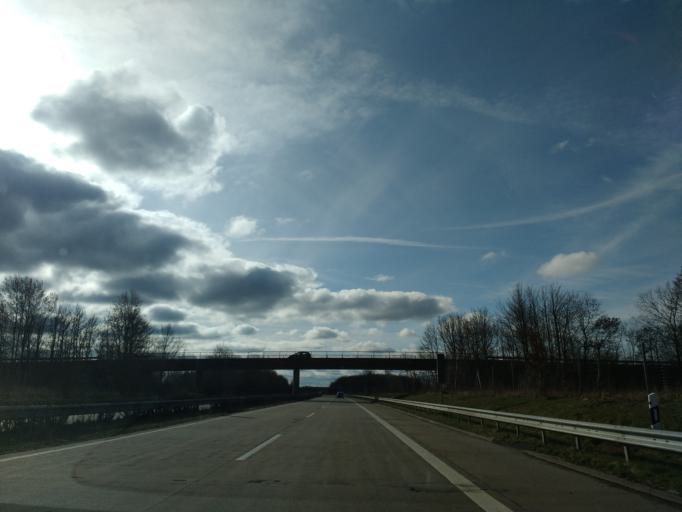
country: DE
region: Lower Saxony
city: Midlum
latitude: 53.6827
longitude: 8.6585
